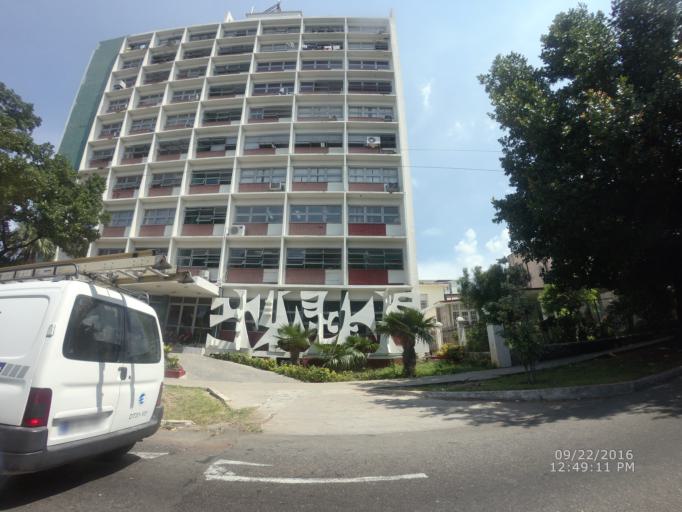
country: CU
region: La Habana
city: Havana
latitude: 23.1338
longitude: -82.3963
